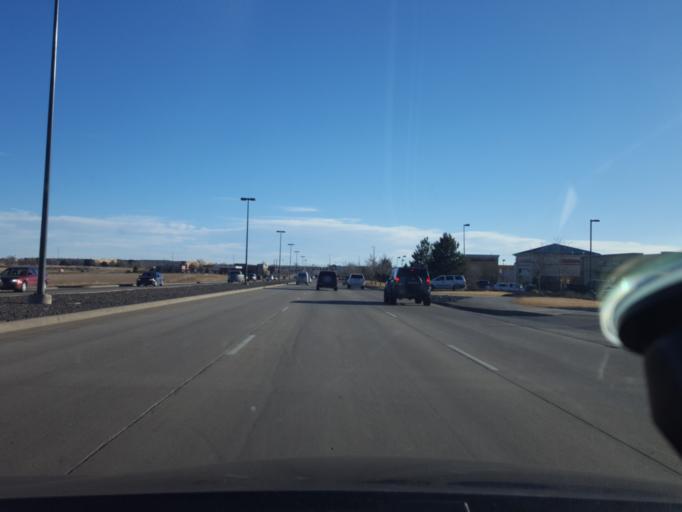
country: US
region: Colorado
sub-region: Adams County
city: Aurora
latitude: 39.7682
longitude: -104.7723
